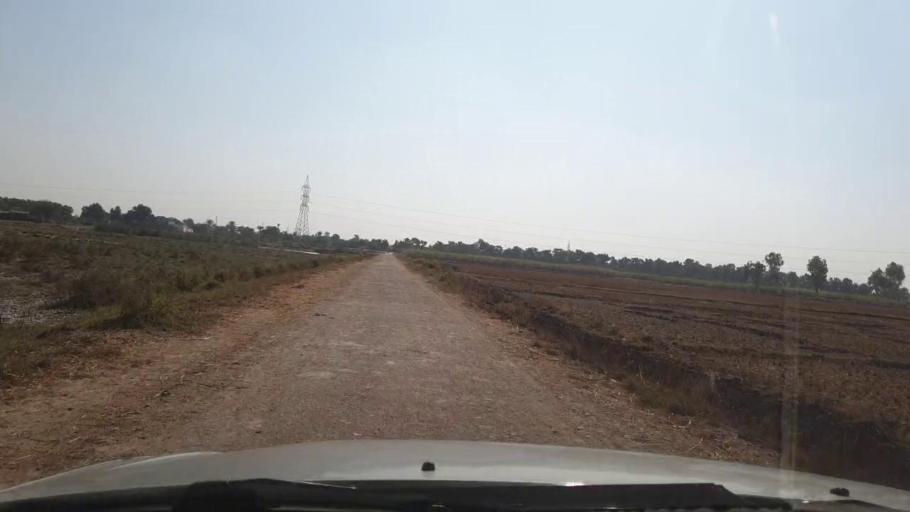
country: PK
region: Sindh
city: Tando Muhammad Khan
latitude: 25.1485
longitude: 68.5360
